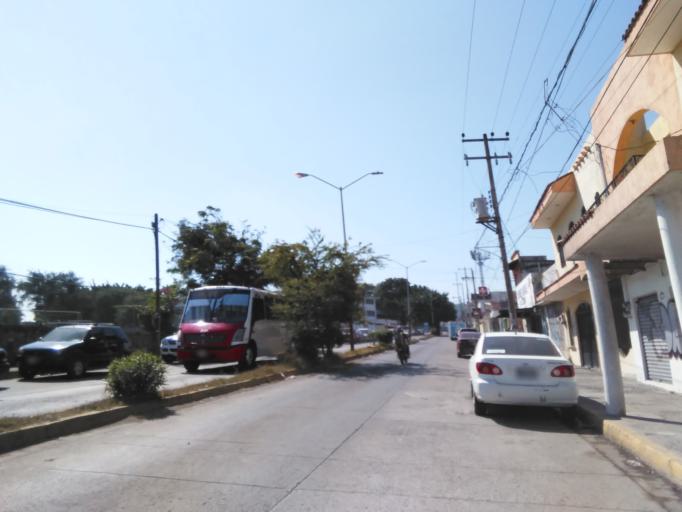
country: MX
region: Nayarit
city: Tepic
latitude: 21.4960
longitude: -104.8937
